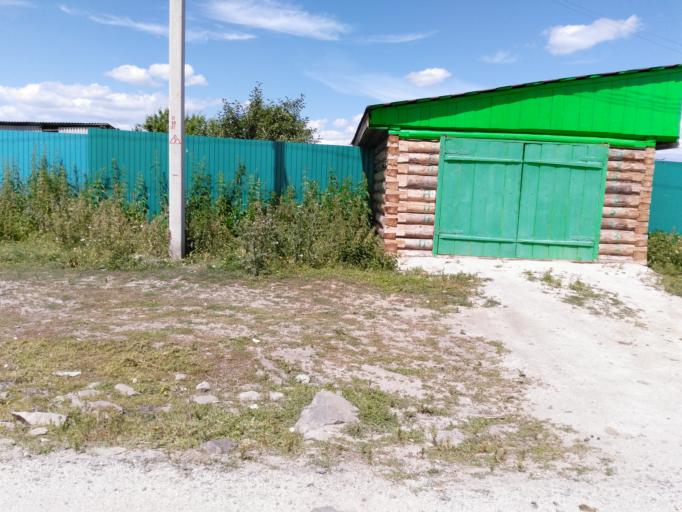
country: RU
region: Bashkortostan
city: Akhunovo
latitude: 54.2036
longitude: 59.5981
